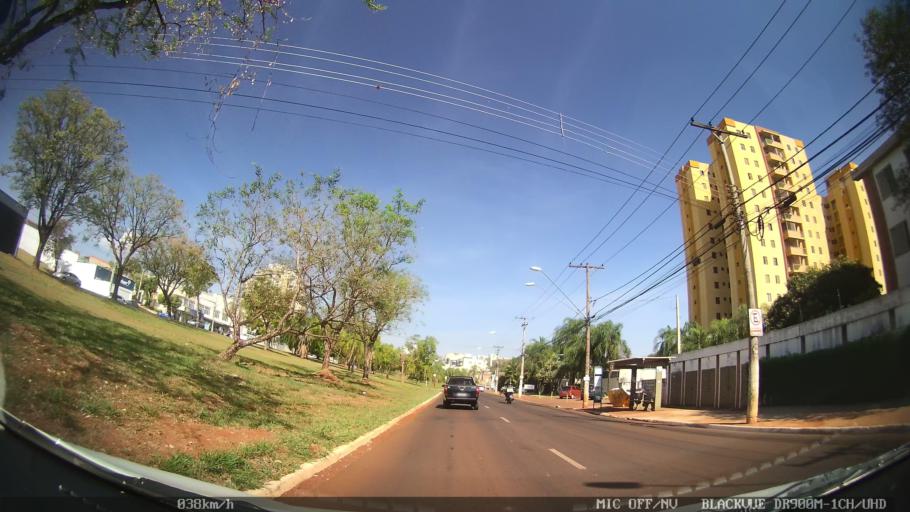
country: BR
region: Sao Paulo
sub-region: Ribeirao Preto
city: Ribeirao Preto
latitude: -21.2002
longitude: -47.8233
